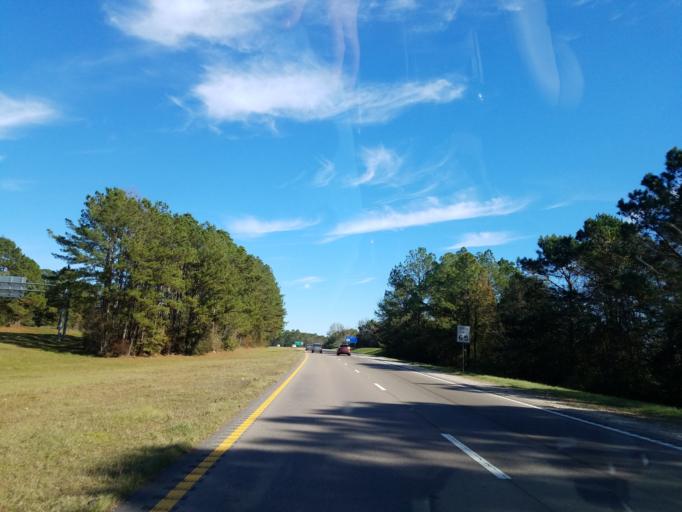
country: US
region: Mississippi
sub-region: Forrest County
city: Hattiesburg
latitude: 31.2378
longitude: -89.3111
